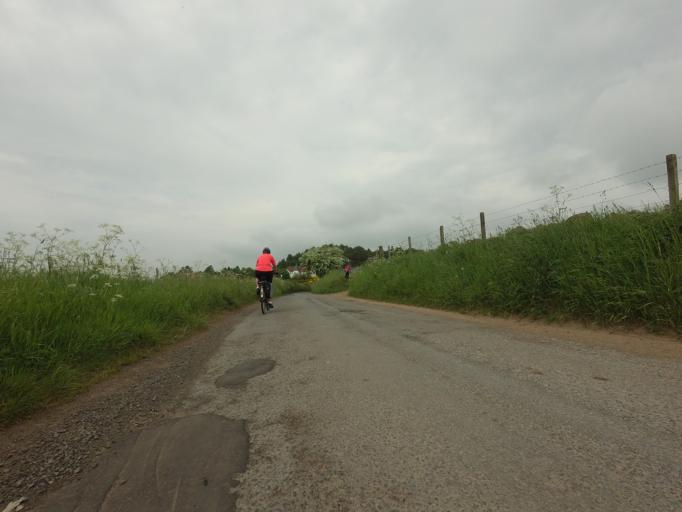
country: GB
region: Scotland
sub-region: Fife
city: Ballingry
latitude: 56.2269
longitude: -3.3413
